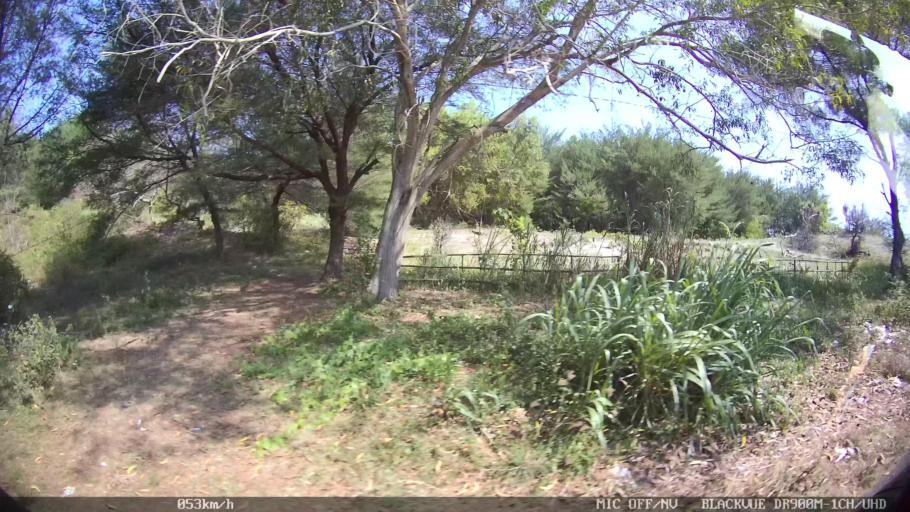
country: ID
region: Daerah Istimewa Yogyakarta
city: Bambanglipuro
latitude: -8.0179
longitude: 110.3124
